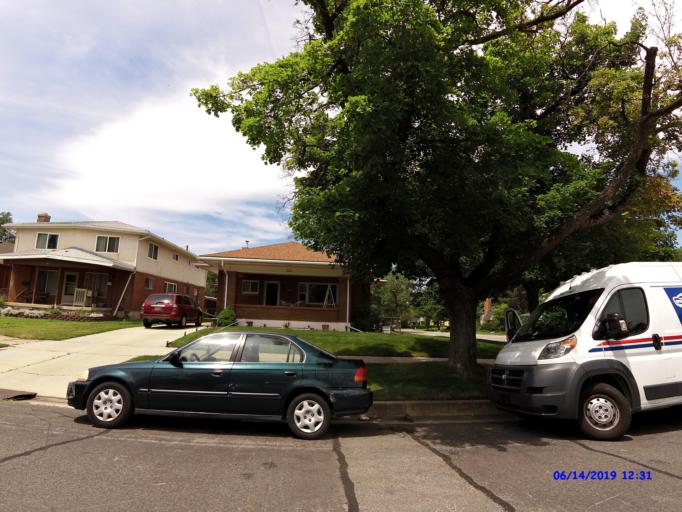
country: US
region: Utah
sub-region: Weber County
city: Ogden
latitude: 41.2182
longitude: -111.9511
